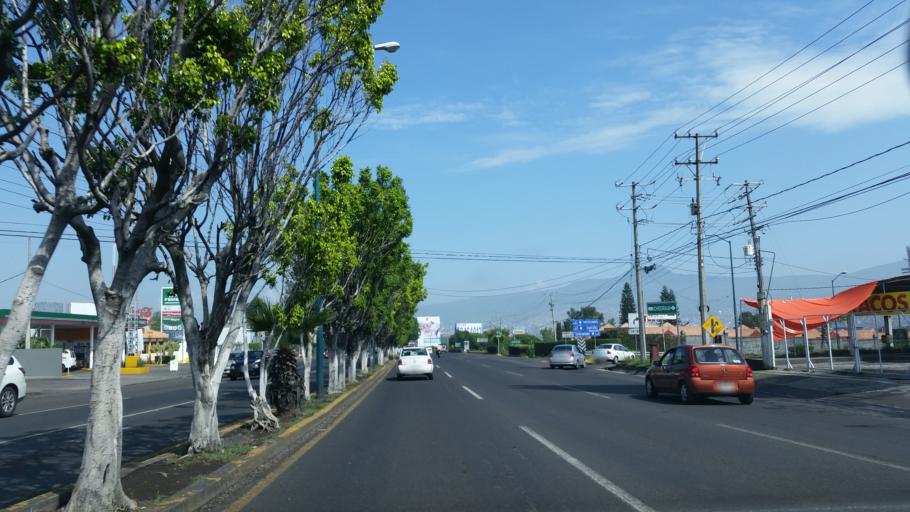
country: MX
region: Michoacan
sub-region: Morelia
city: Morelos
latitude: 19.6757
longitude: -101.2172
